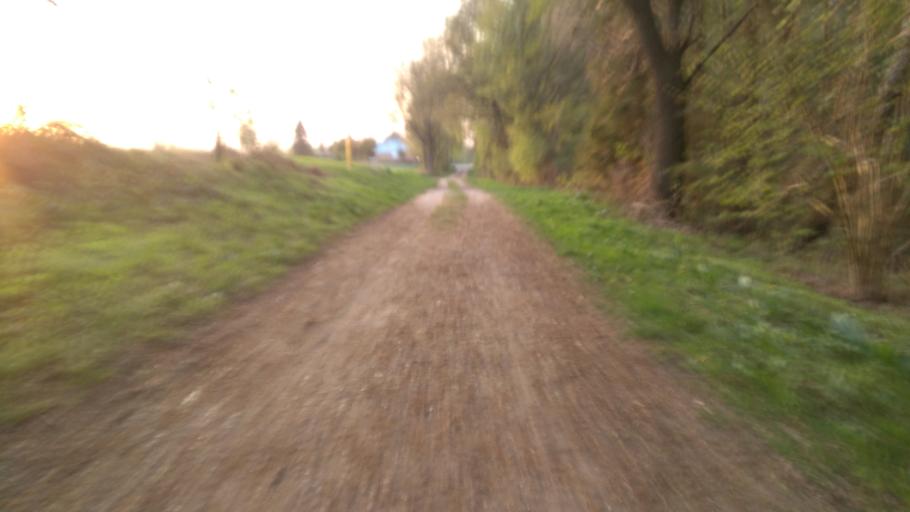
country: DE
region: Lower Saxony
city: Harsefeld
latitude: 53.4789
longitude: 9.5196
